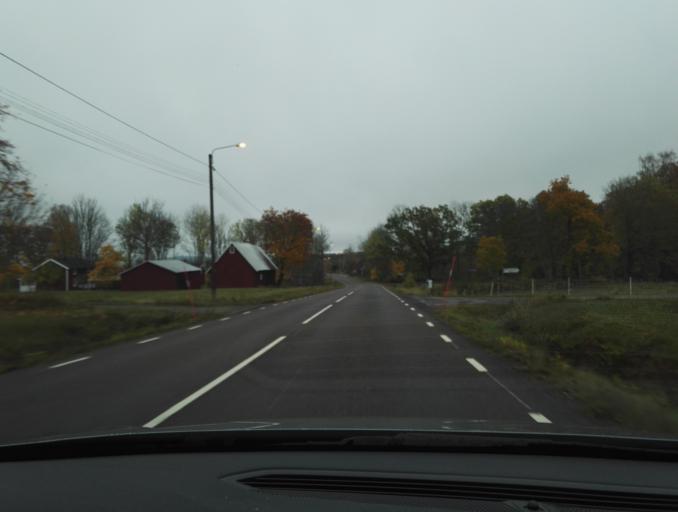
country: SE
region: Kronoberg
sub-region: Vaxjo Kommun
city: Rottne
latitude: 57.0240
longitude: 14.8448
